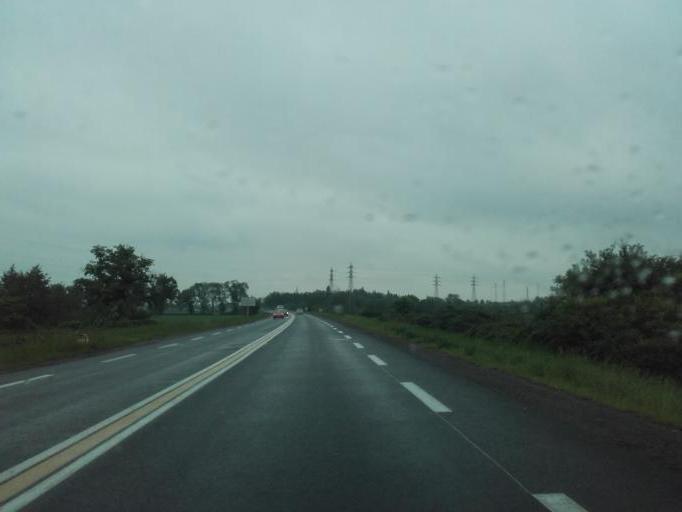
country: FR
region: Bourgogne
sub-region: Departement de Saone-et-Loire
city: Charnay-les-Macon
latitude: 46.2924
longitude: 4.7736
